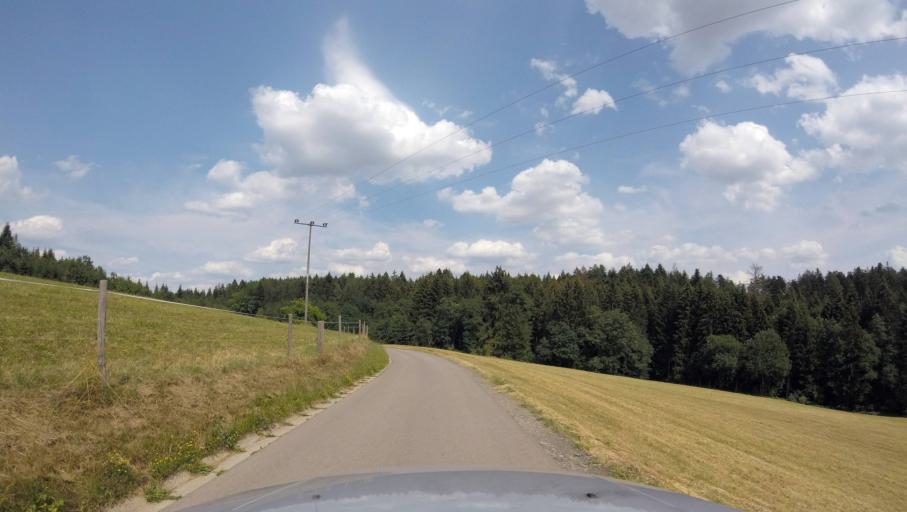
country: DE
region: Baden-Wuerttemberg
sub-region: Regierungsbezirk Stuttgart
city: Spraitbach
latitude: 48.8672
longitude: 9.7486
